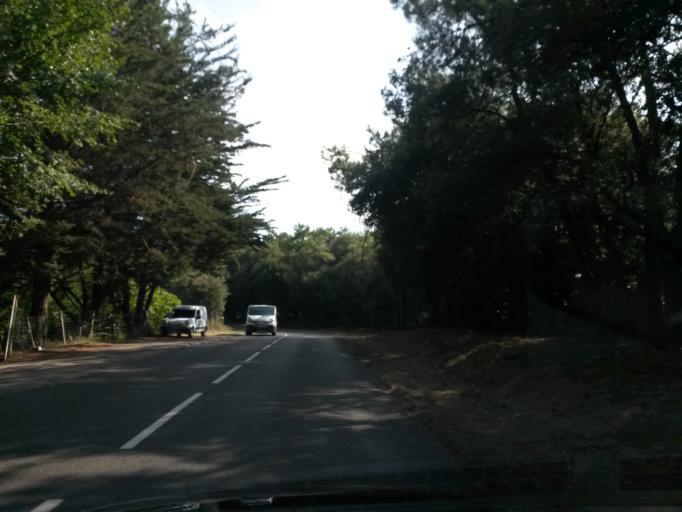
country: FR
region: Pays de la Loire
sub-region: Departement de la Vendee
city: Olonne-sur-Mer
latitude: 46.5302
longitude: -1.8121
